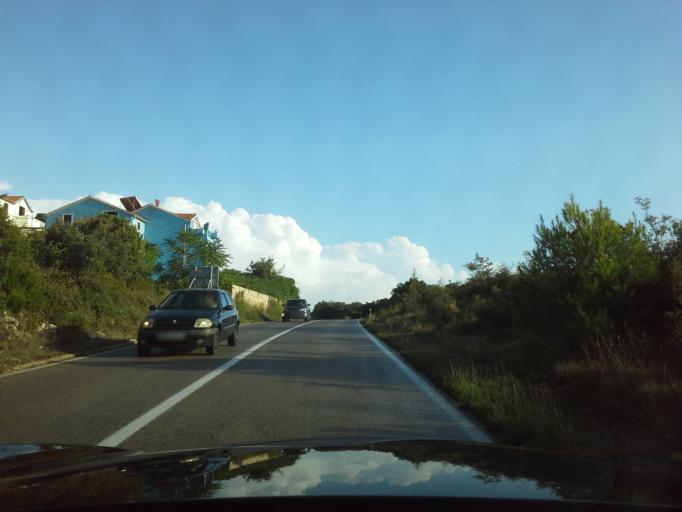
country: HR
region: Primorsko-Goranska
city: Mali Losinj
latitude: 44.5866
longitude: 14.4094
